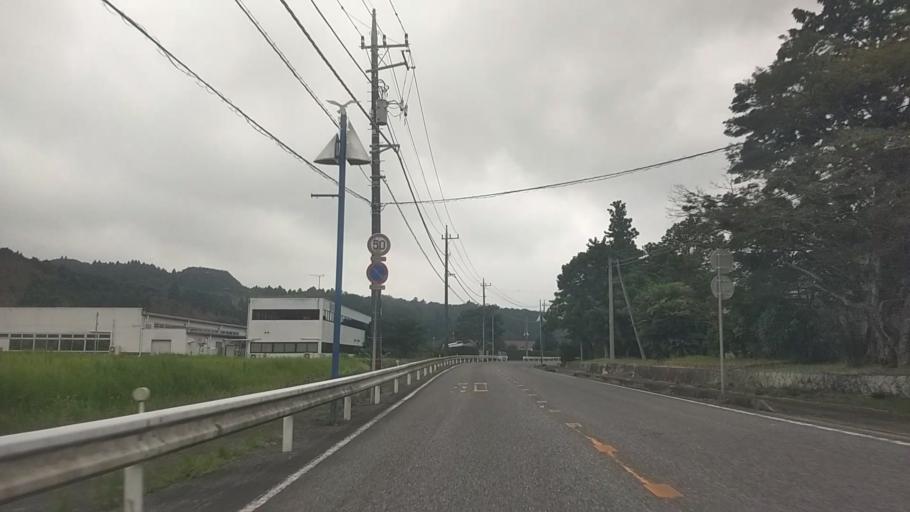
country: JP
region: Chiba
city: Kawaguchi
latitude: 35.1430
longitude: 139.9626
